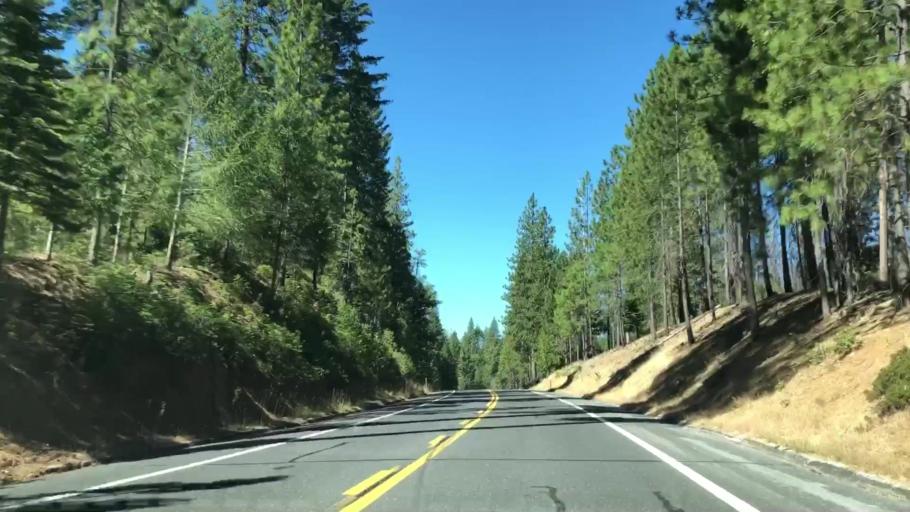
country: US
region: California
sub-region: Mariposa County
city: Midpines
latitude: 37.8135
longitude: -119.8907
